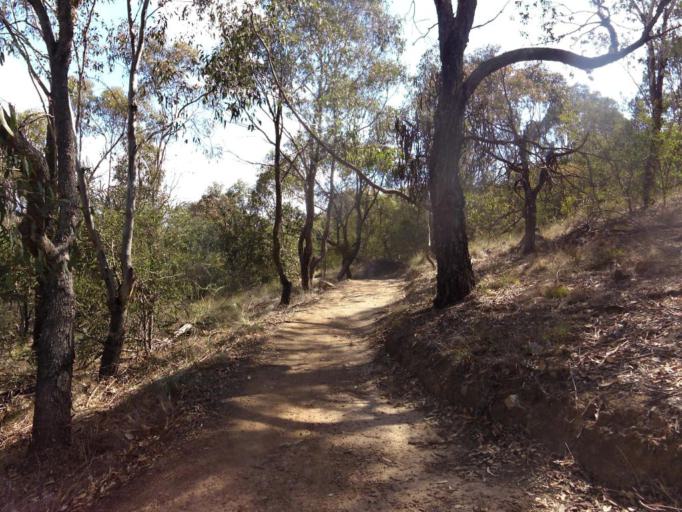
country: AU
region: Australian Capital Territory
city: Belconnen
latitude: -35.1590
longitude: 149.0771
